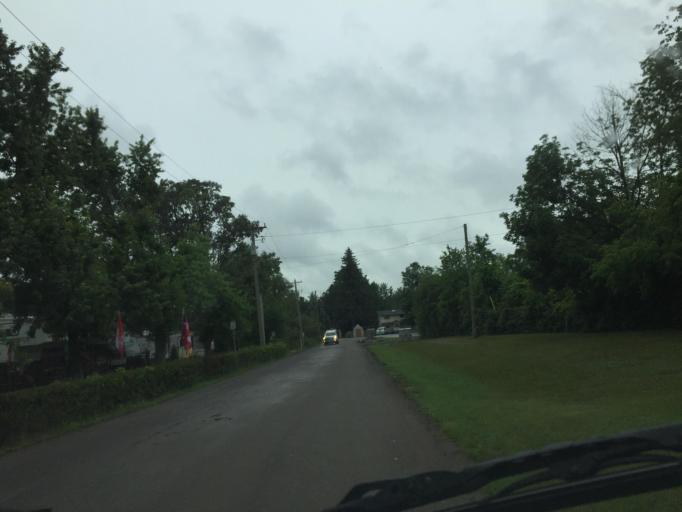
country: CA
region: Ontario
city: Cambridge
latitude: 43.4231
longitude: -80.2628
